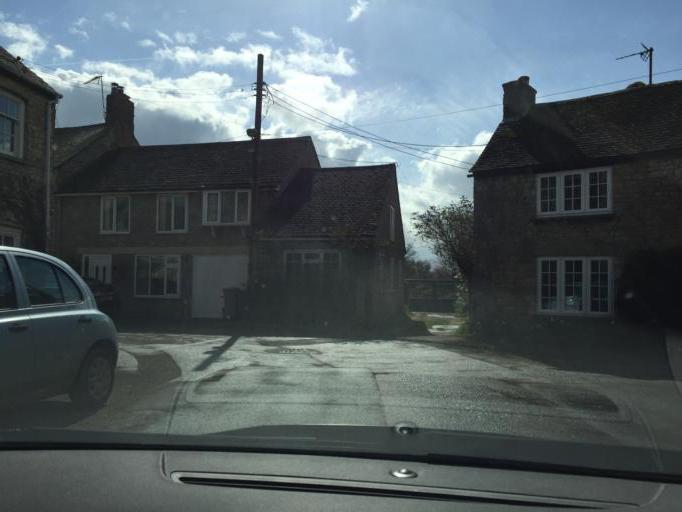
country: GB
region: England
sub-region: Oxfordshire
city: Woodstock
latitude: 51.8761
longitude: -1.3653
